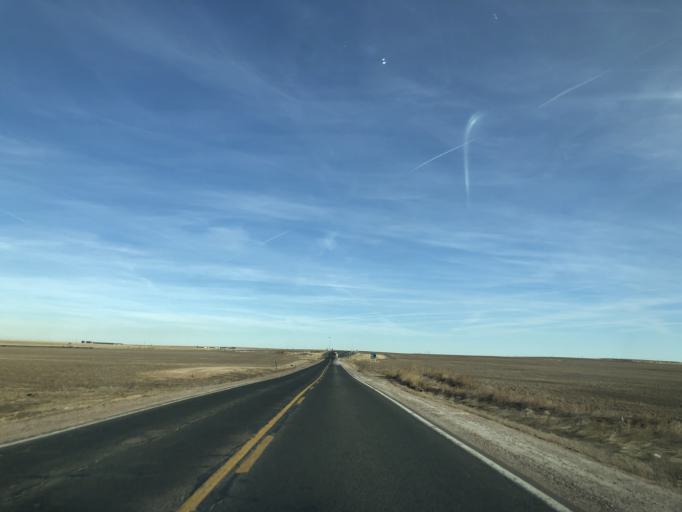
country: US
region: Colorado
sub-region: Adams County
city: Aurora
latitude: 39.7984
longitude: -104.7254
